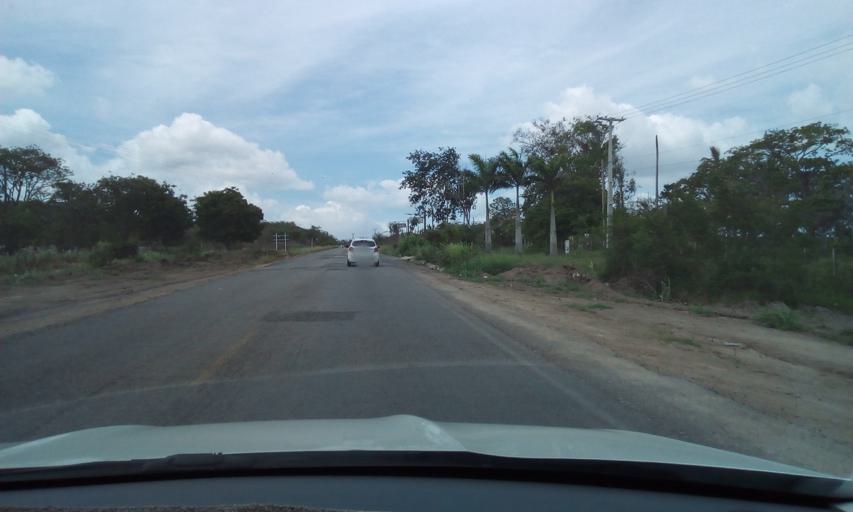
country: BR
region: Pernambuco
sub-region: Bezerros
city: Bezerros
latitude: -8.2798
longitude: -35.7424
